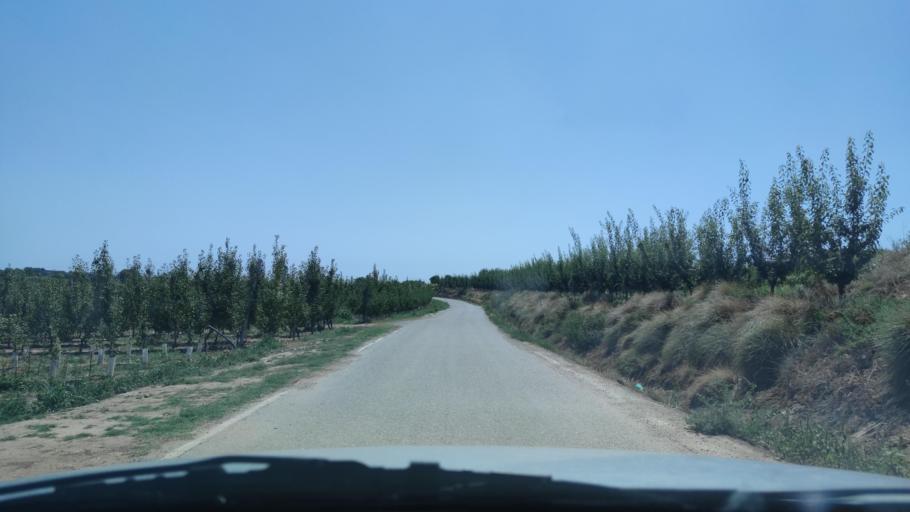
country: ES
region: Catalonia
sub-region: Provincia de Lleida
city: Torrefarrera
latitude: 41.6436
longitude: 0.5911
